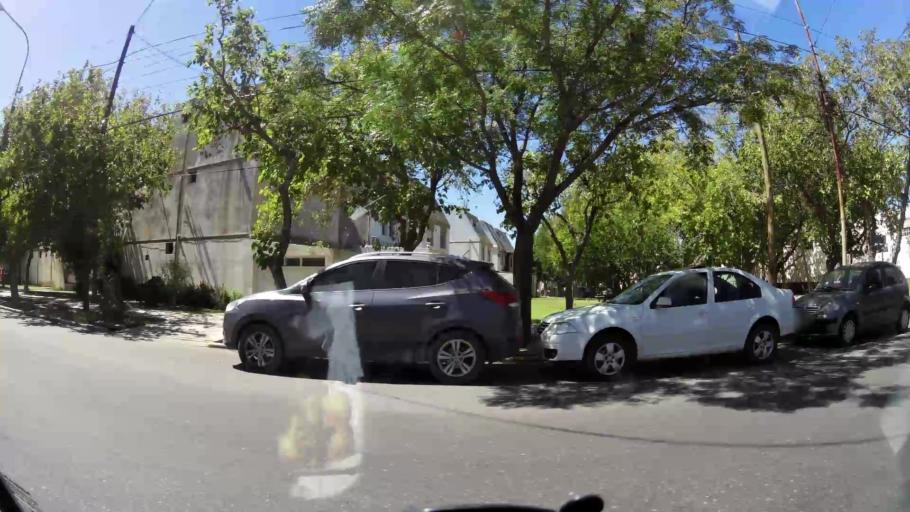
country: AR
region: San Juan
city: San Juan
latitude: -31.5279
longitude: -68.5223
